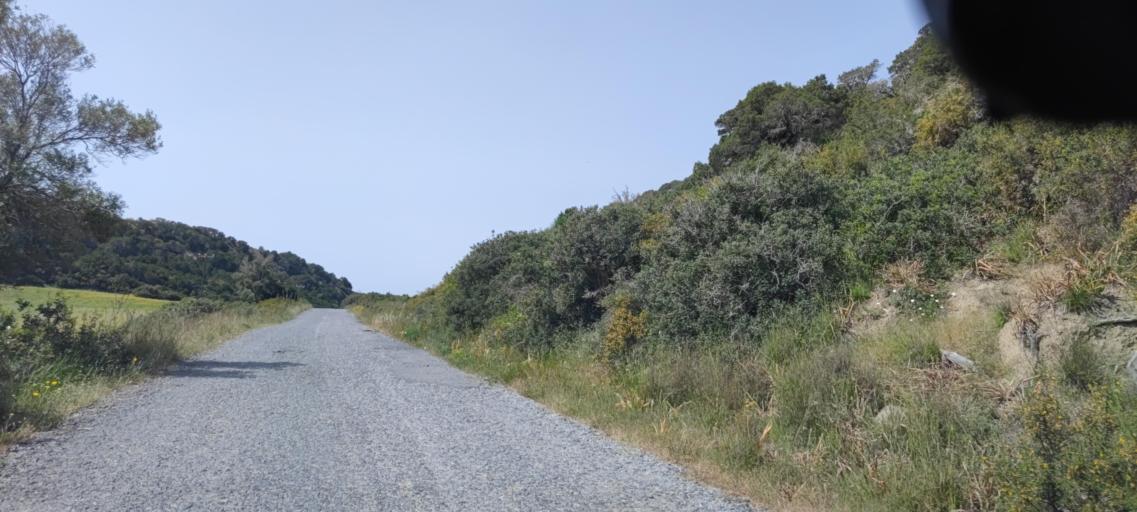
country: CY
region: Ammochostos
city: Rizokarpaso
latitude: 35.6201
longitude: 34.4717
